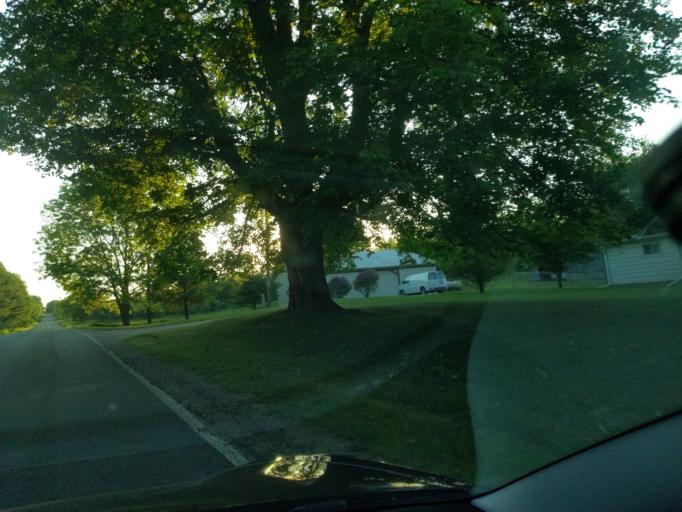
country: US
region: Michigan
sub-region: Barry County
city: Nashville
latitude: 42.5380
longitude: -85.1061
